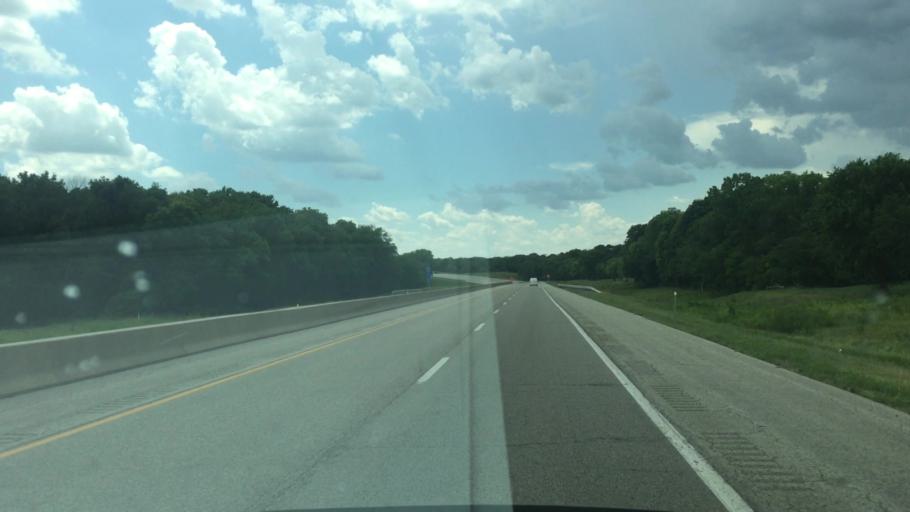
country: US
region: Kansas
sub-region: Shawnee County
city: Auburn
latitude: 38.9301
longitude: -95.7633
